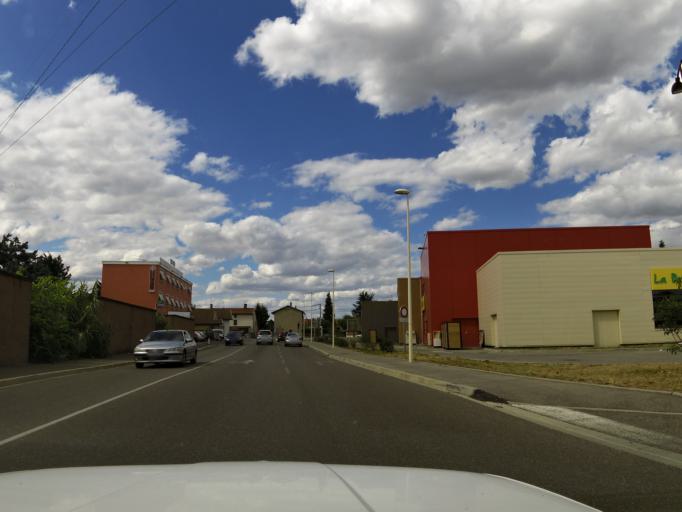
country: FR
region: Rhone-Alpes
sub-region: Departement de l'Isere
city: Pont-de-Cheruy
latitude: 45.7487
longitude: 5.1849
